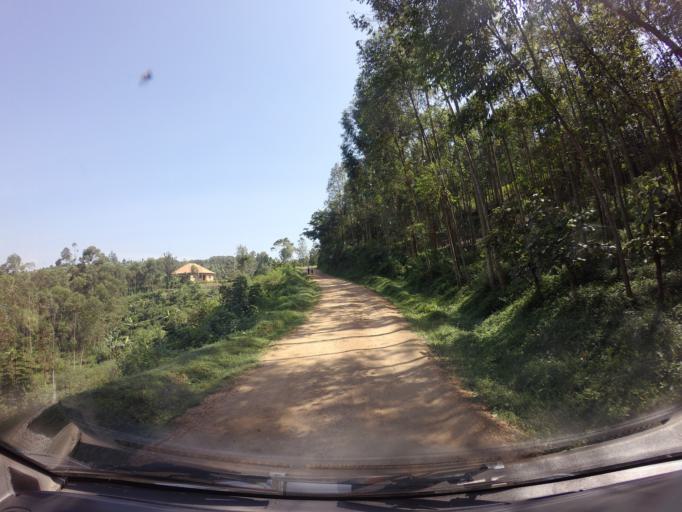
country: UG
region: Western Region
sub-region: Kanungu District
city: Kanungu
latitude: -0.8347
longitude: 29.7781
